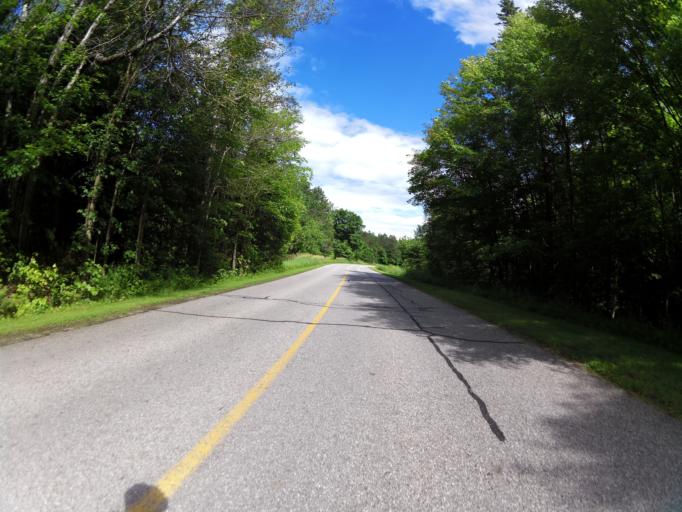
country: CA
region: Quebec
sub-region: Outaouais
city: Wakefield
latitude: 45.6253
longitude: -76.0121
